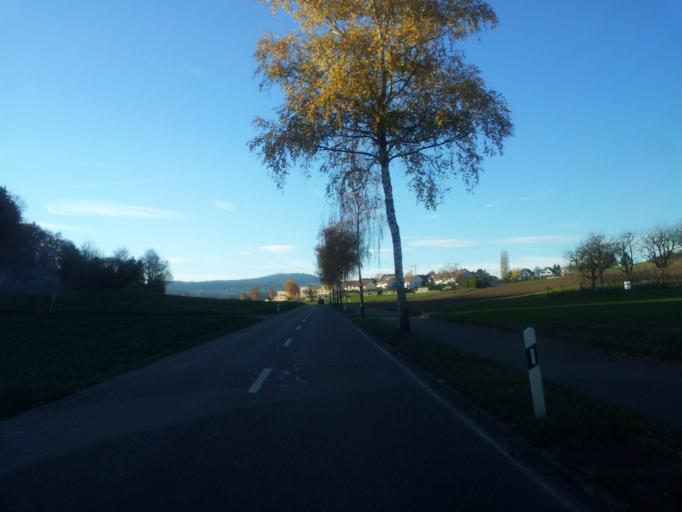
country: CH
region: Zurich
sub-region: Bezirk Dielsdorf
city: Oberglatt / Bahnhofquartier
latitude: 47.4645
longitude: 8.5086
